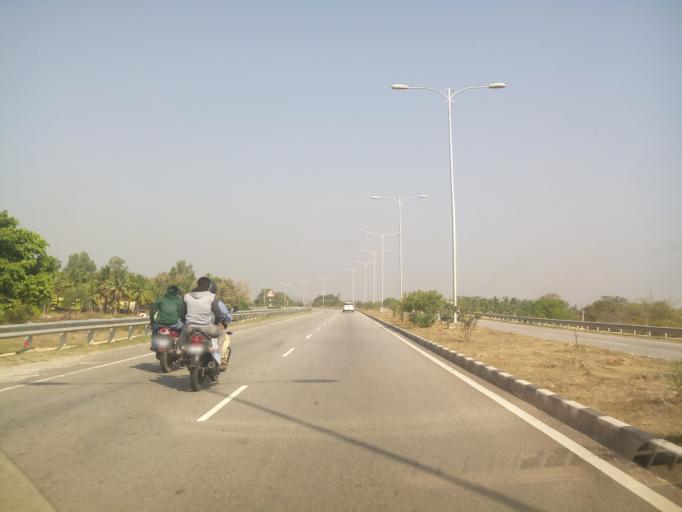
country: IN
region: Karnataka
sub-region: Tumkur
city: Kunigal
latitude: 13.0030
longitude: 77.0168
